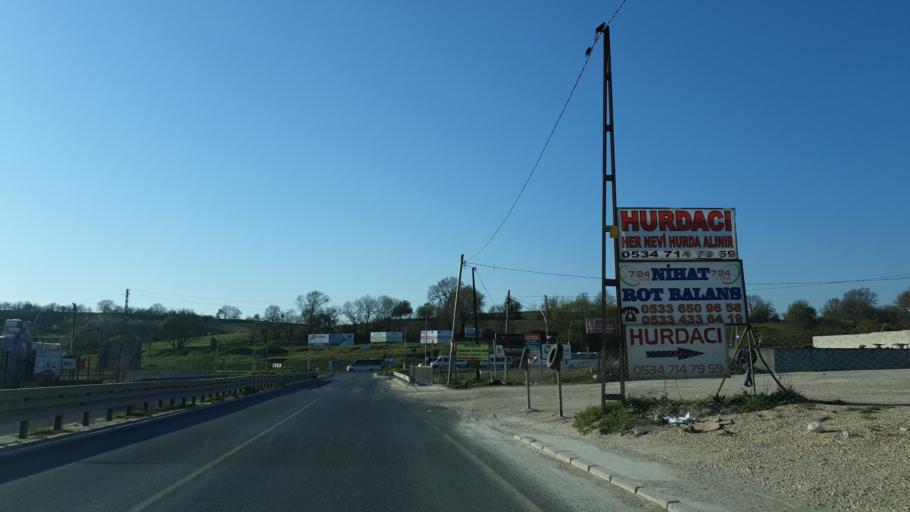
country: TR
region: Tekirdag
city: Cerkezkoey
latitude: 41.2766
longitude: 27.9862
